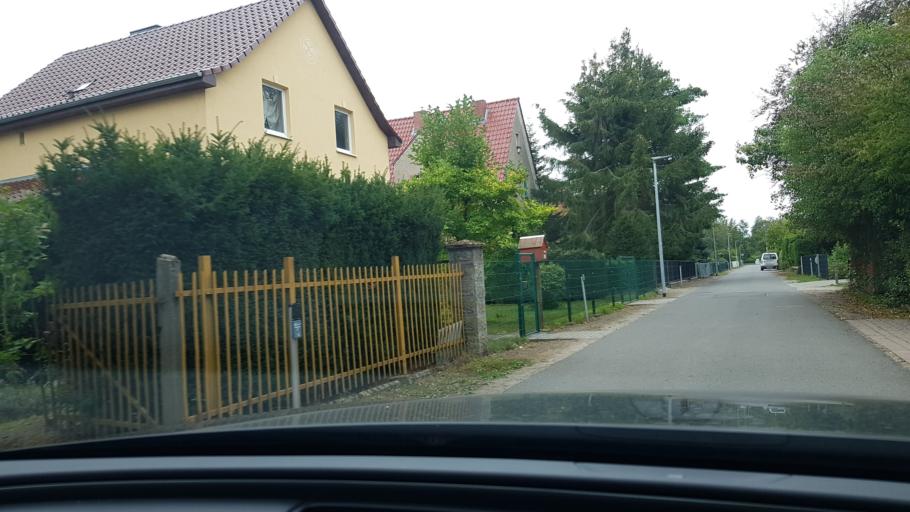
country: DE
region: Brandenburg
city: Brieselang
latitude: 52.5863
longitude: 12.9997
